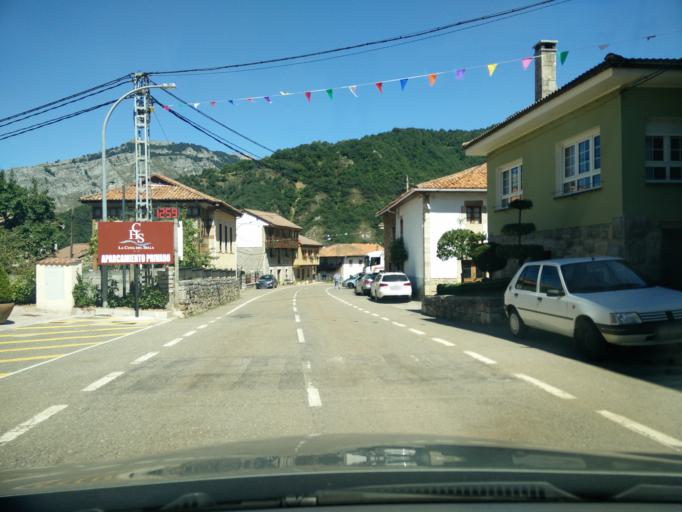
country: ES
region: Castille and Leon
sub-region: Provincia de Leon
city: Oseja de Sajambre
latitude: 43.1371
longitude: -5.0384
